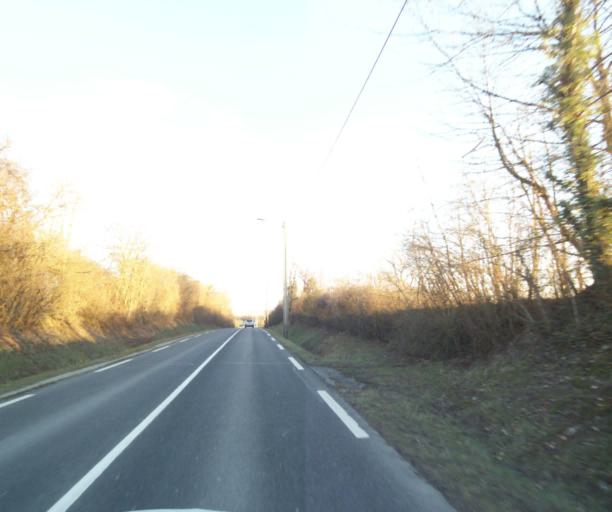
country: FR
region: Lorraine
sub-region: Departement de Meurthe-et-Moselle
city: Laneuveville-devant-Nancy
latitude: 48.6663
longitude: 6.2347
